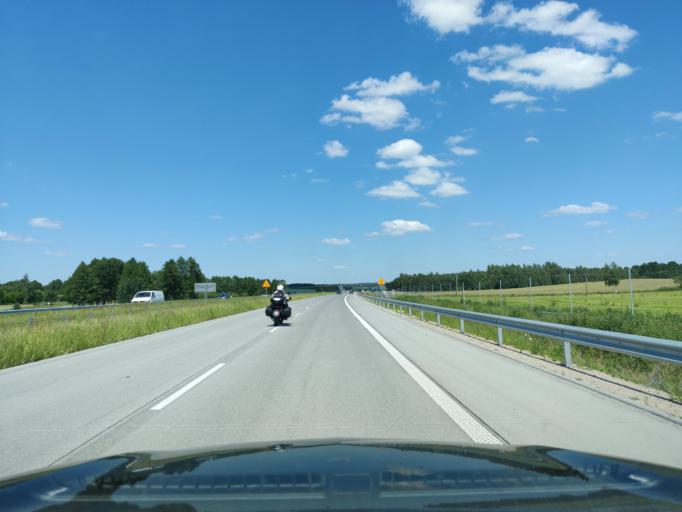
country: PL
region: Masovian Voivodeship
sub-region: Powiat mlawski
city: Strzegowo
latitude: 52.9575
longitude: 20.3060
